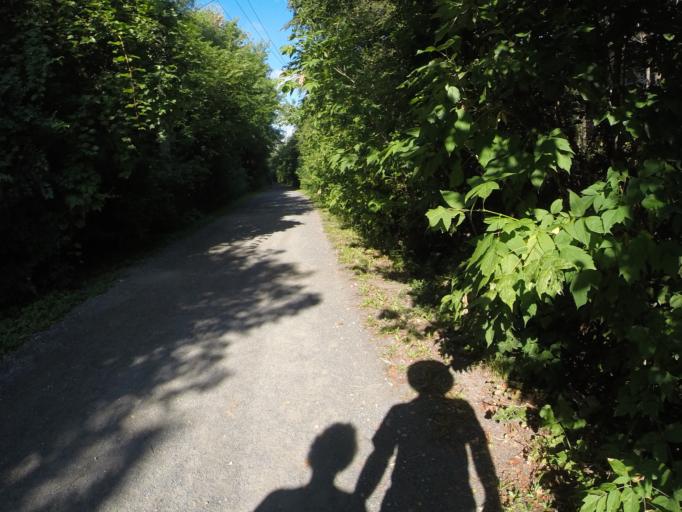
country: CA
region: Ontario
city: Toronto
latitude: 43.7048
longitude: -79.4262
